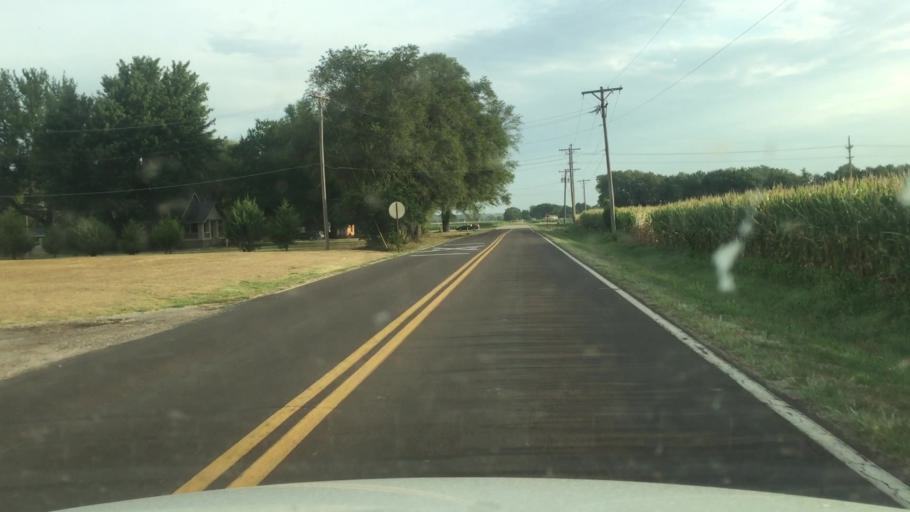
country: US
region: Kansas
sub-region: Shawnee County
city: Topeka
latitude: 39.0573
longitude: -95.6131
